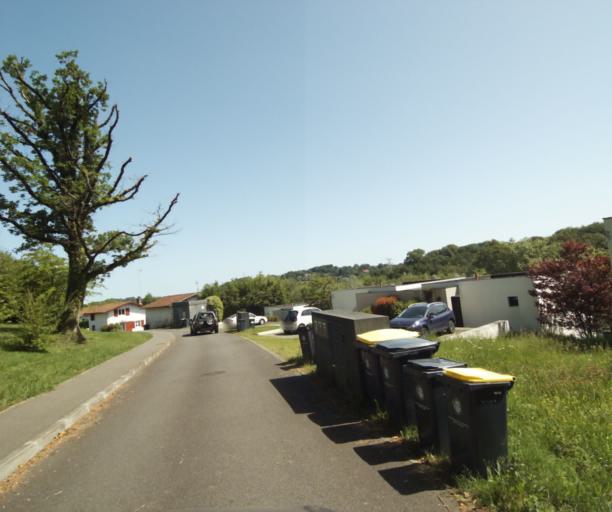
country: FR
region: Aquitaine
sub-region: Departement des Pyrenees-Atlantiques
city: Mouguerre
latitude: 43.4727
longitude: -1.4443
